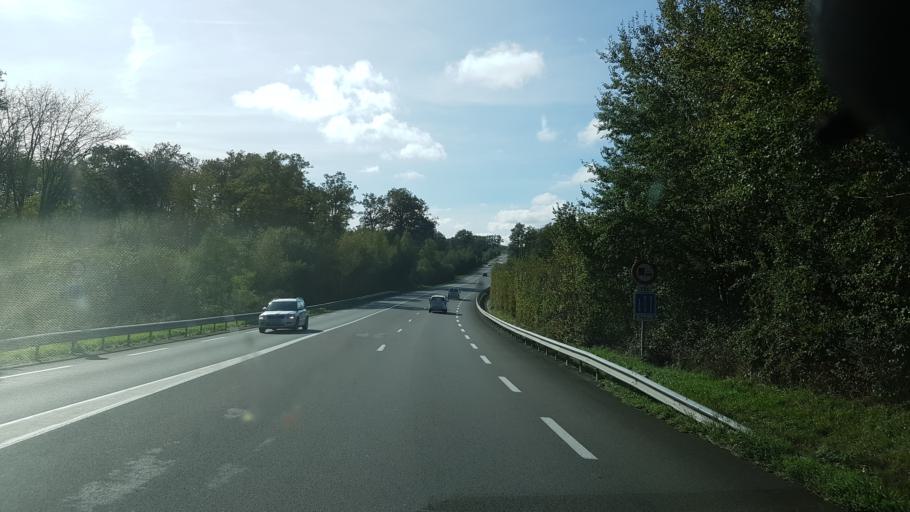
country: FR
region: Poitou-Charentes
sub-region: Departement de la Charente
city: Saint-Claud
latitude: 45.9180
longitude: 0.5096
